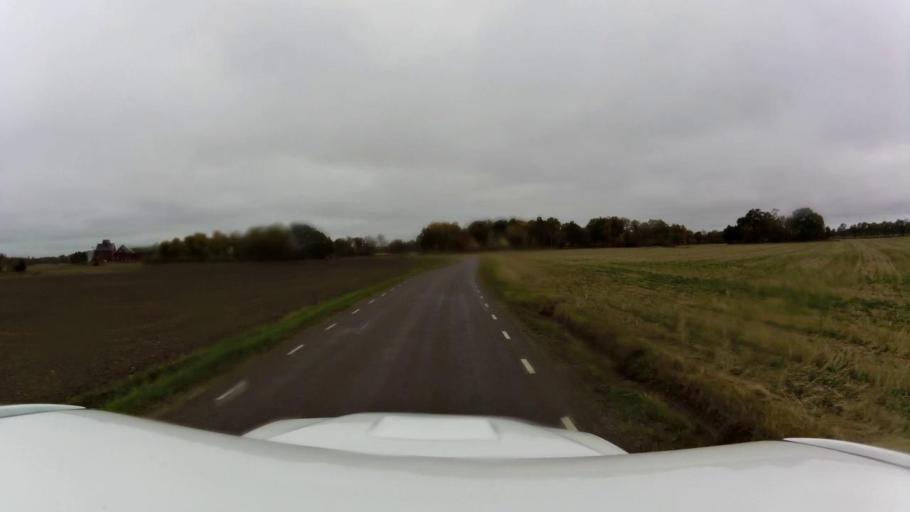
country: SE
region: OEstergoetland
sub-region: Linkopings Kommun
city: Linghem
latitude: 58.4806
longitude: 15.7303
